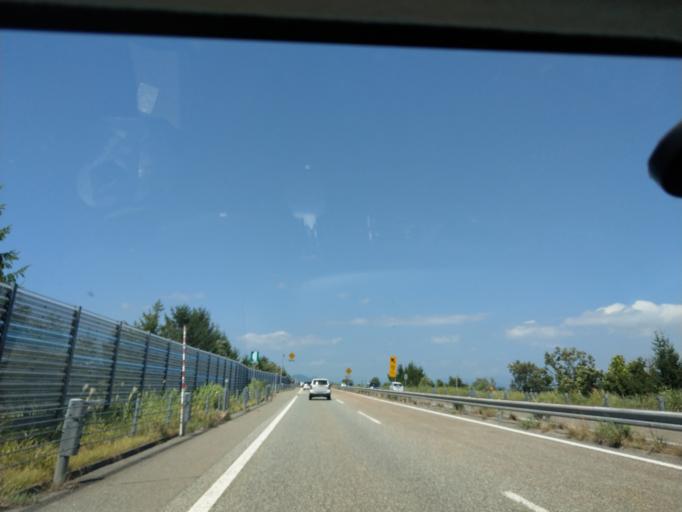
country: JP
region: Akita
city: Yokotemachi
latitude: 39.3679
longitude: 140.4862
